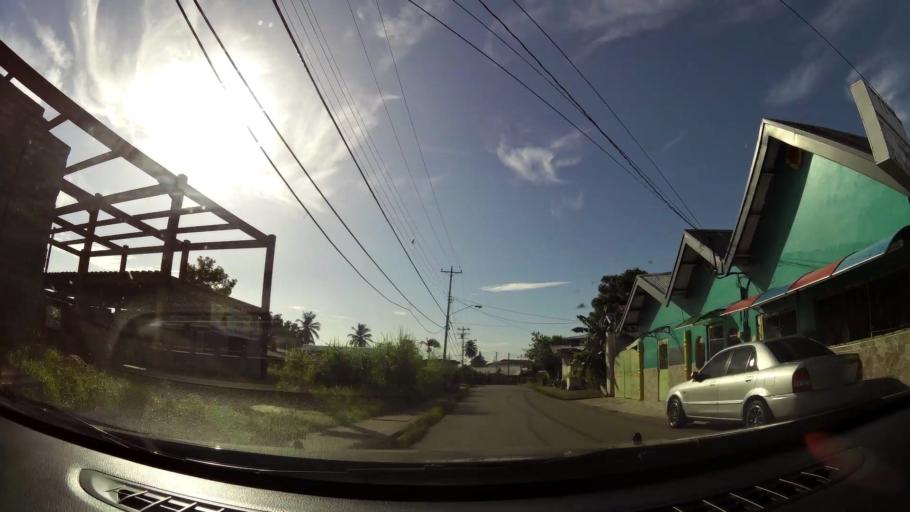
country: TT
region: Chaguanas
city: Chaguanas
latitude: 10.5252
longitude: -61.3861
